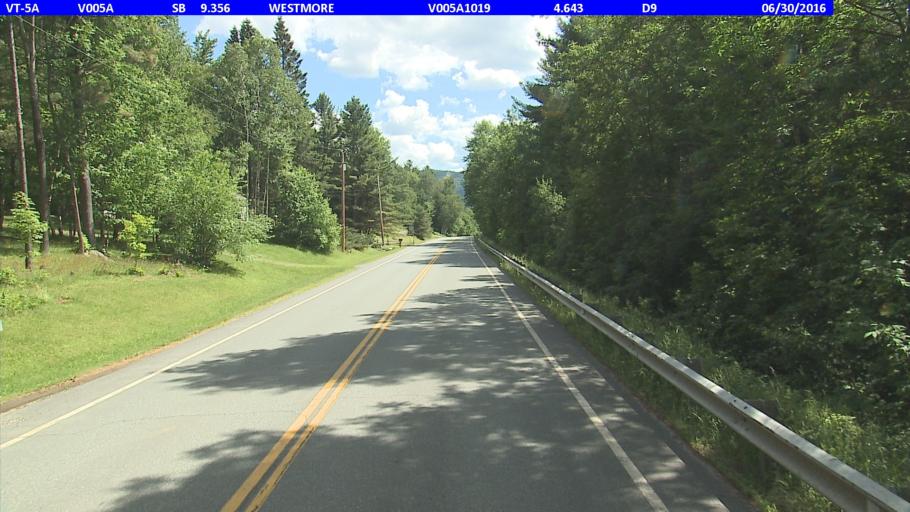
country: US
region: Vermont
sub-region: Caledonia County
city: Lyndonville
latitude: 44.7574
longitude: -72.0523
